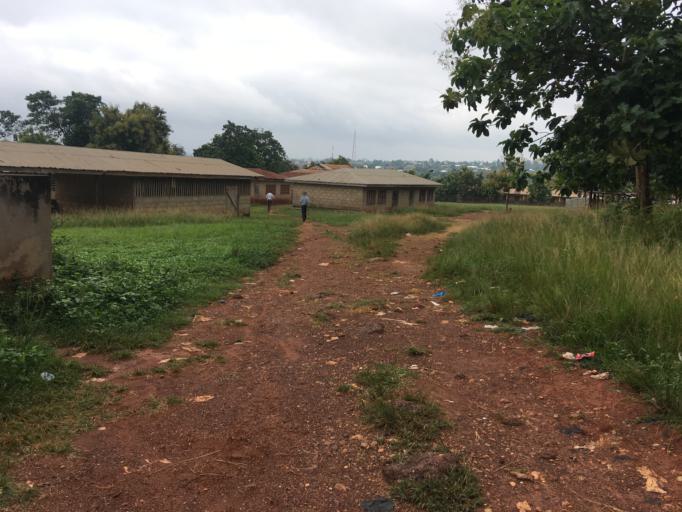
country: GH
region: Western
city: Bibiani
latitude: 6.8015
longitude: -2.5188
